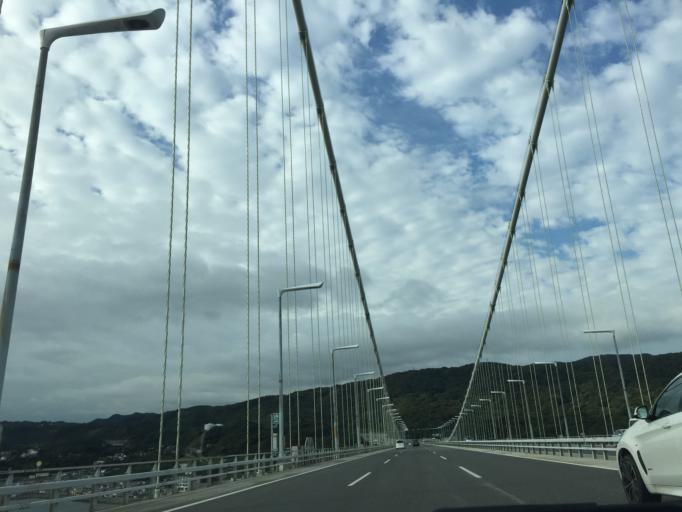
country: JP
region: Hyogo
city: Akashi
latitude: 34.6063
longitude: 135.0121
